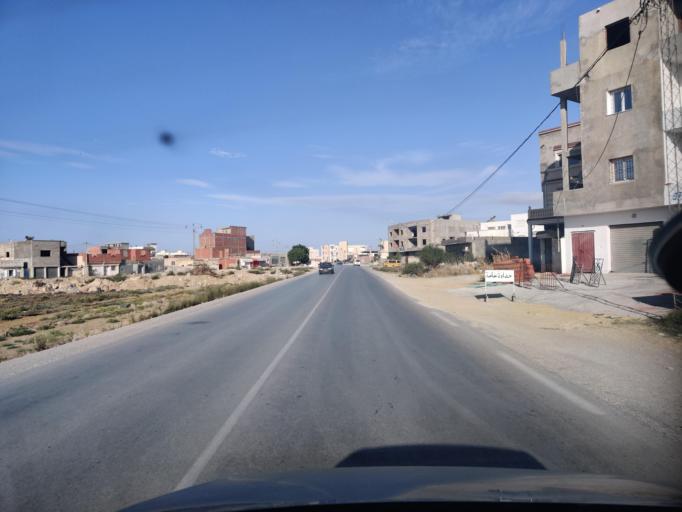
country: TN
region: Ariana
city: Ariana
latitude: 36.9557
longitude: 10.2251
